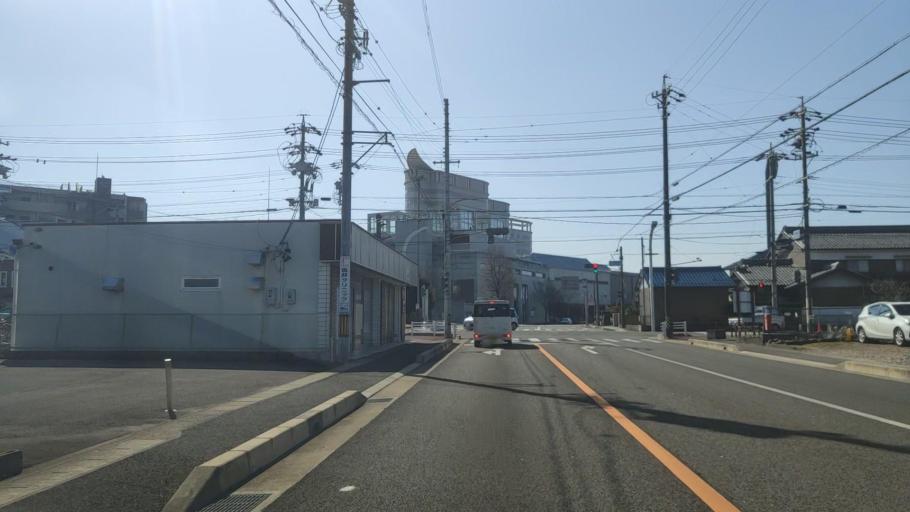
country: JP
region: Gifu
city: Gifu-shi
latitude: 35.4429
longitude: 136.7684
